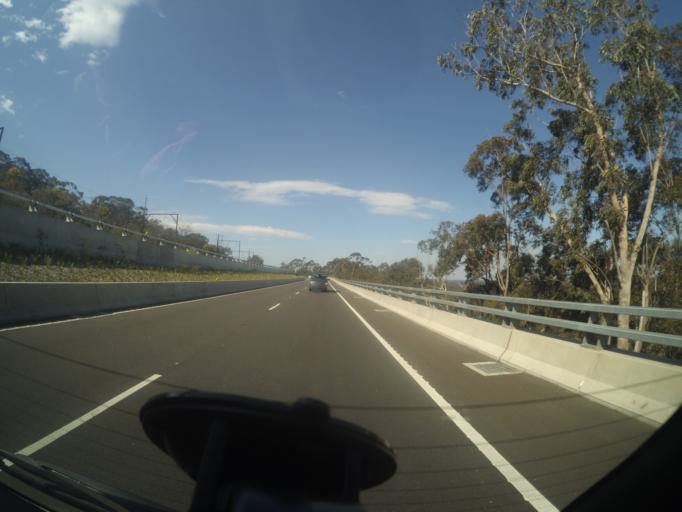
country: AU
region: New South Wales
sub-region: Blue Mountains Municipality
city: Lawson
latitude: -33.7257
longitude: 150.3975
